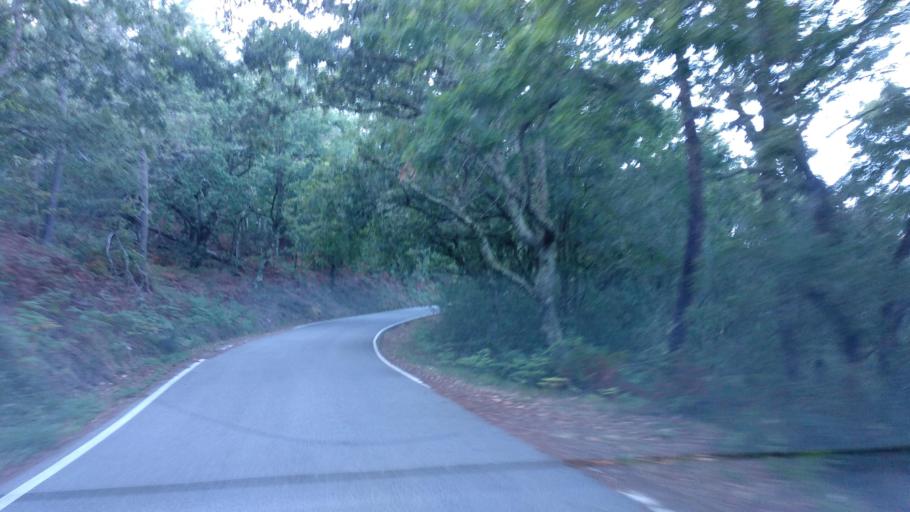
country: ES
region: Galicia
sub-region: Provincia de Pontevedra
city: Fornelos de Montes
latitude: 42.3504
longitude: -8.4896
